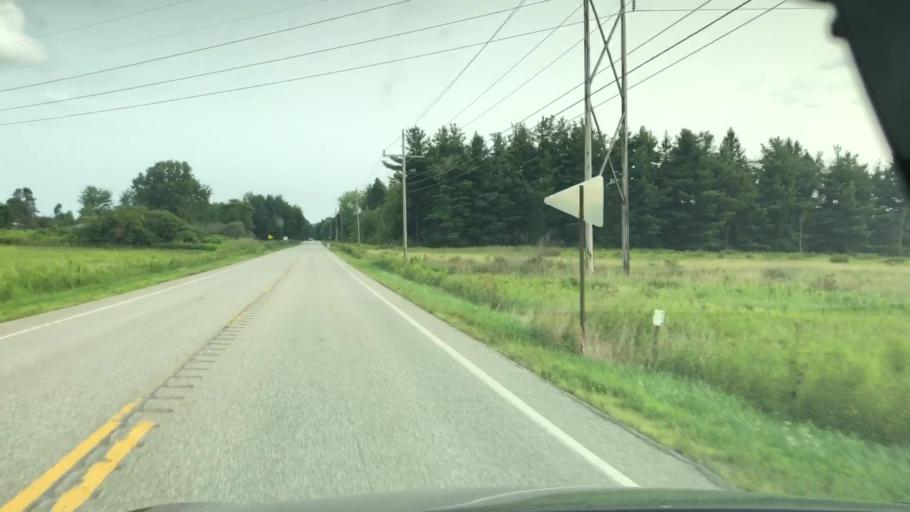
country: US
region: Pennsylvania
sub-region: Erie County
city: Union City
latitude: 41.9307
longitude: -79.8437
